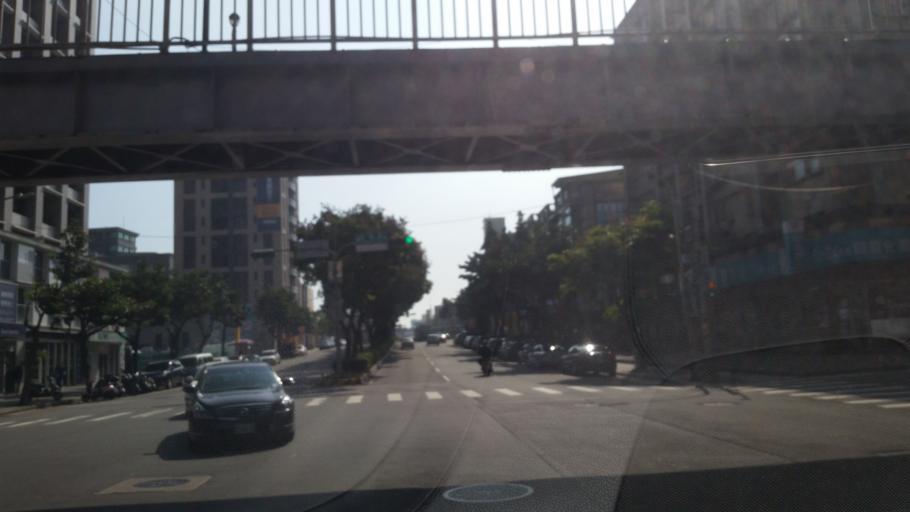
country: TW
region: Taiwan
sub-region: Taoyuan
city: Taoyuan
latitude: 25.0708
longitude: 121.3698
